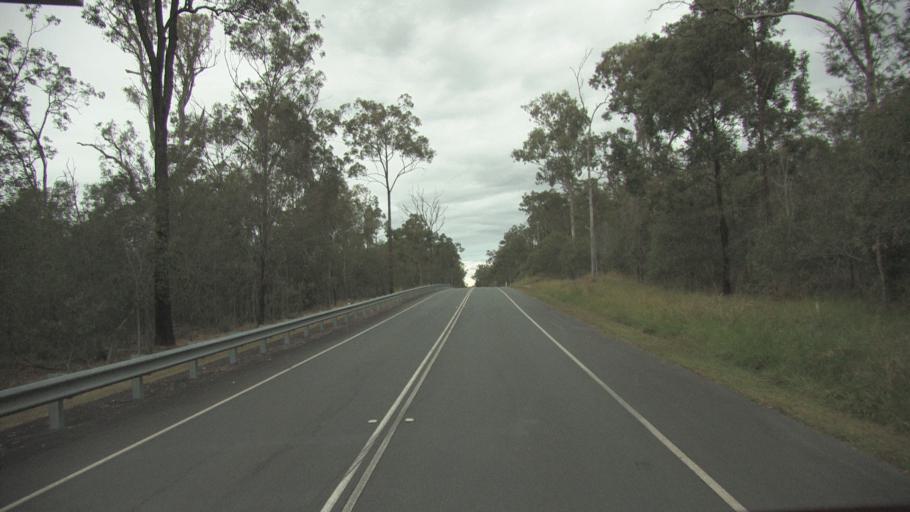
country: AU
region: Queensland
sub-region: Logan
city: Park Ridge South
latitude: -27.7414
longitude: 153.0259
